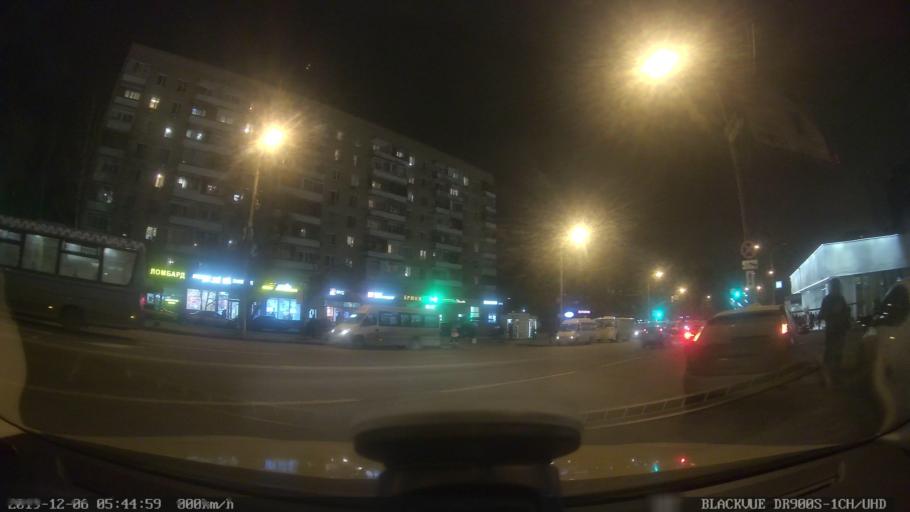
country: RU
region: Moscow
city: Vatutino
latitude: 55.8868
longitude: 37.6617
